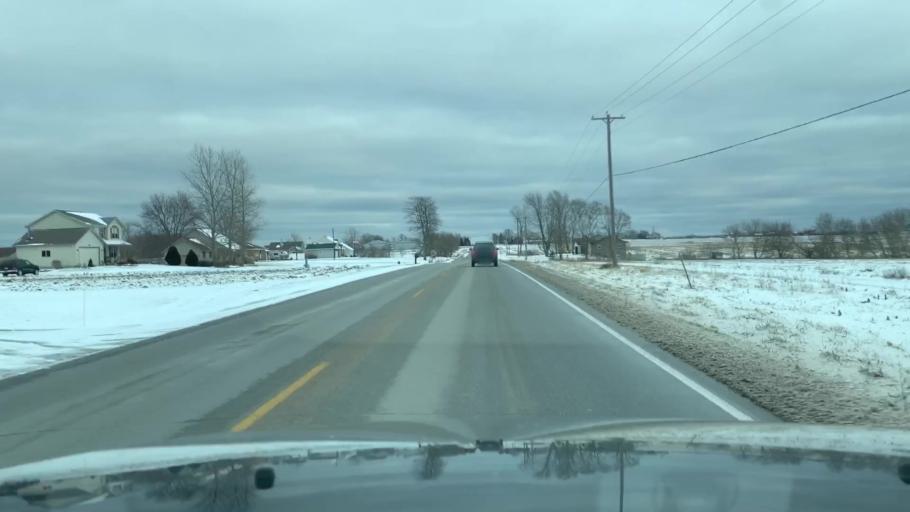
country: US
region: Michigan
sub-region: Ottawa County
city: Zeeland
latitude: 42.8119
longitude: -85.9353
